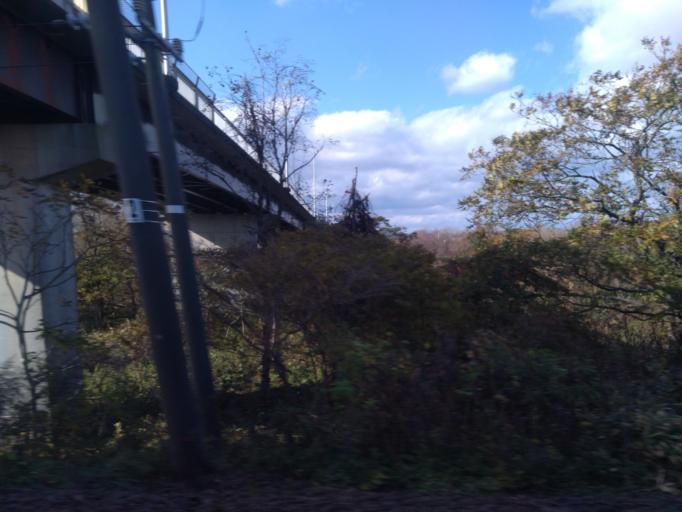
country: JP
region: Hokkaido
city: Shiraoi
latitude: 42.5455
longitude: 141.3449
